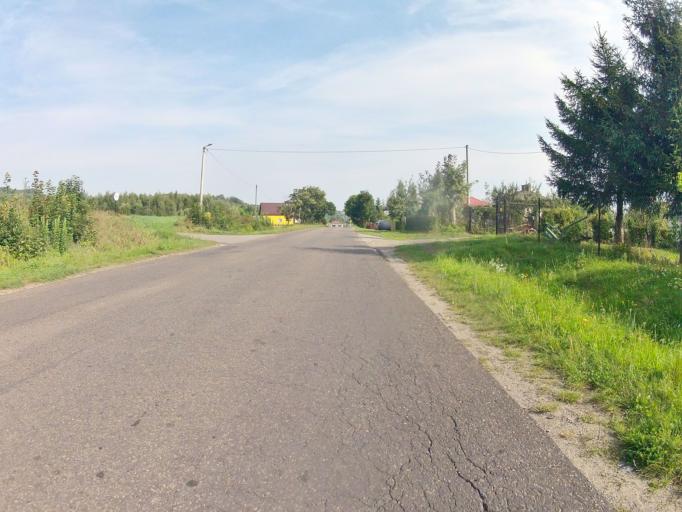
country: PL
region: Subcarpathian Voivodeship
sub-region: Powiat jasielski
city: Brzyska
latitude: 49.7923
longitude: 21.3983
